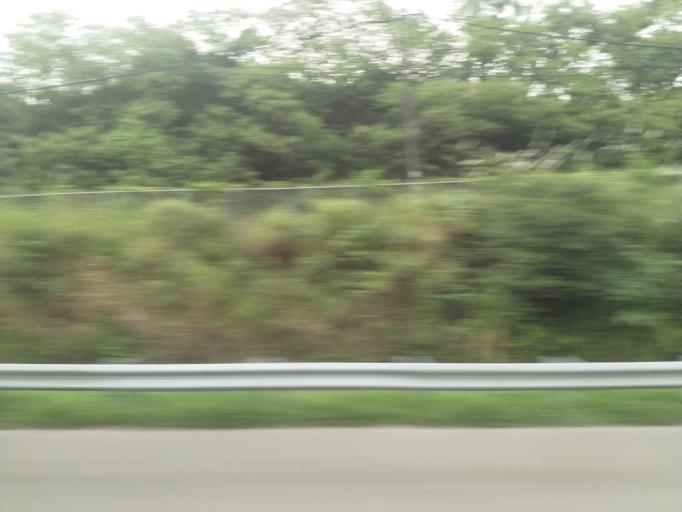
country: TW
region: Taiwan
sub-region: Pingtung
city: Pingtung
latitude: 22.7670
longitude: 120.3980
